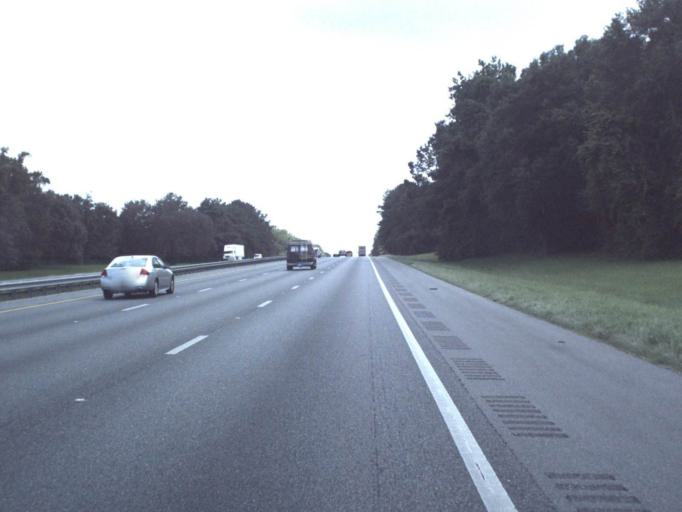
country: US
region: Florida
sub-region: Alachua County
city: High Springs
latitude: 29.9610
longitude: -82.5720
